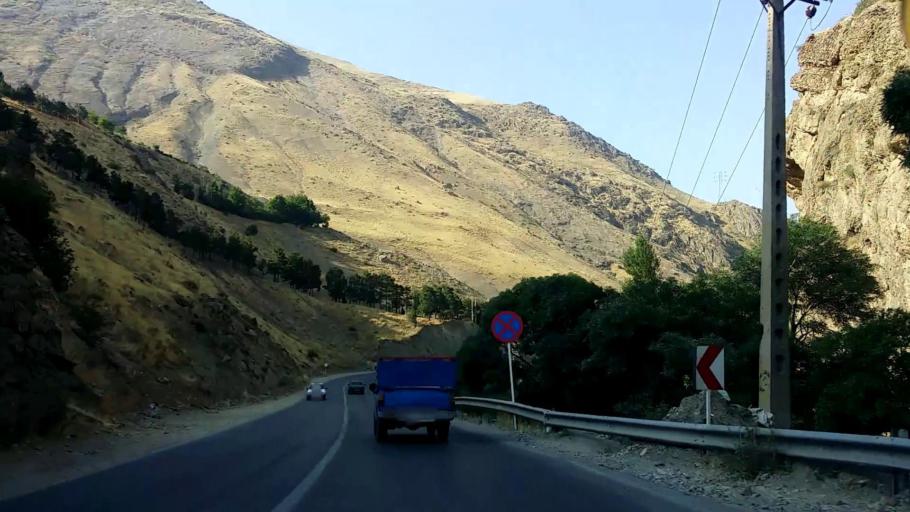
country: IR
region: Alborz
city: Karaj
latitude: 35.9200
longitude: 51.0500
